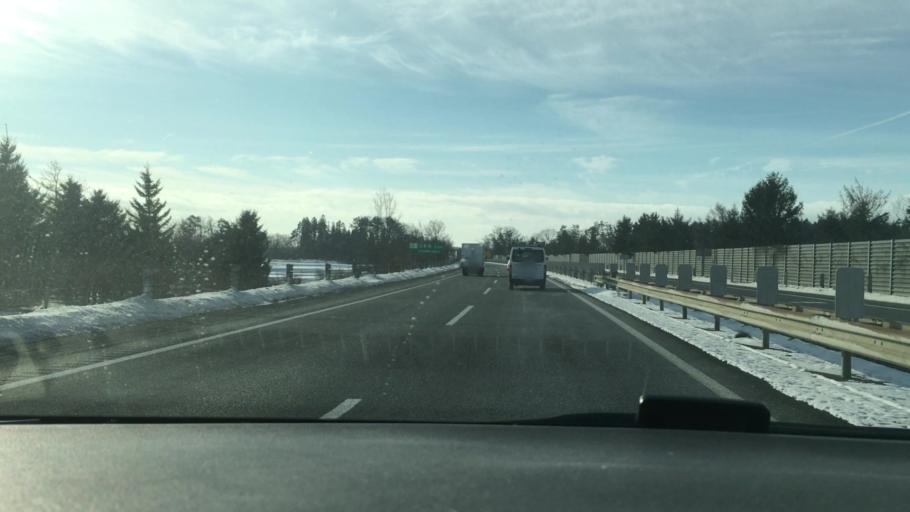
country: JP
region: Iwate
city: Hanamaki
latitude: 39.4063
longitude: 141.0927
